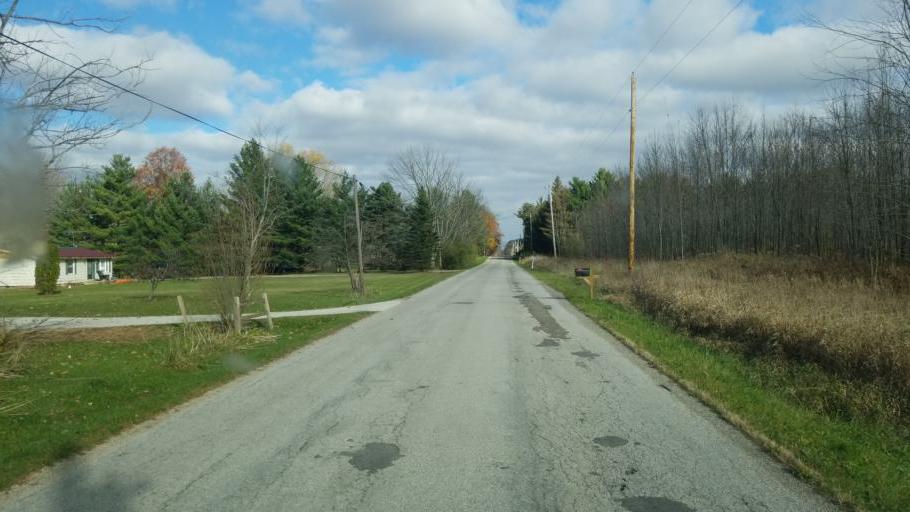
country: US
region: Ohio
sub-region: Crawford County
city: Galion
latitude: 40.6500
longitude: -82.7469
